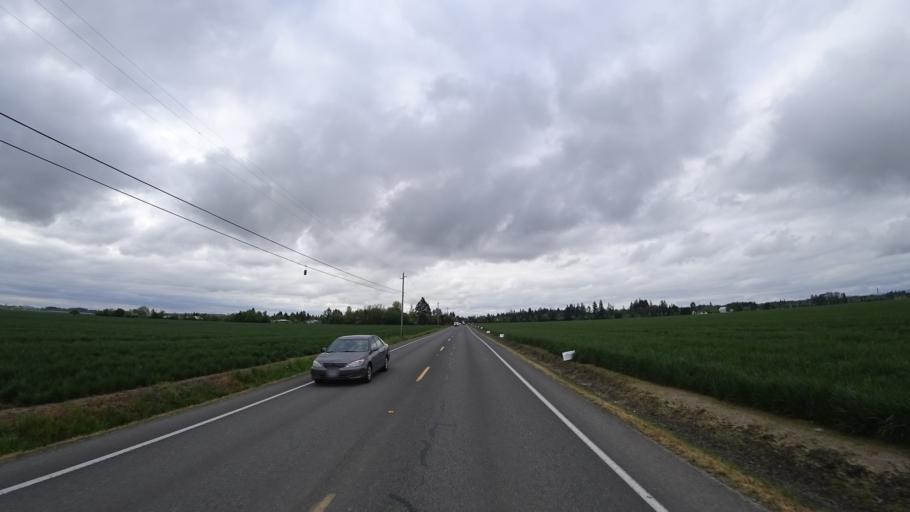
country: US
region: Oregon
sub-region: Washington County
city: Hillsboro
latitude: 45.5558
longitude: -122.9732
